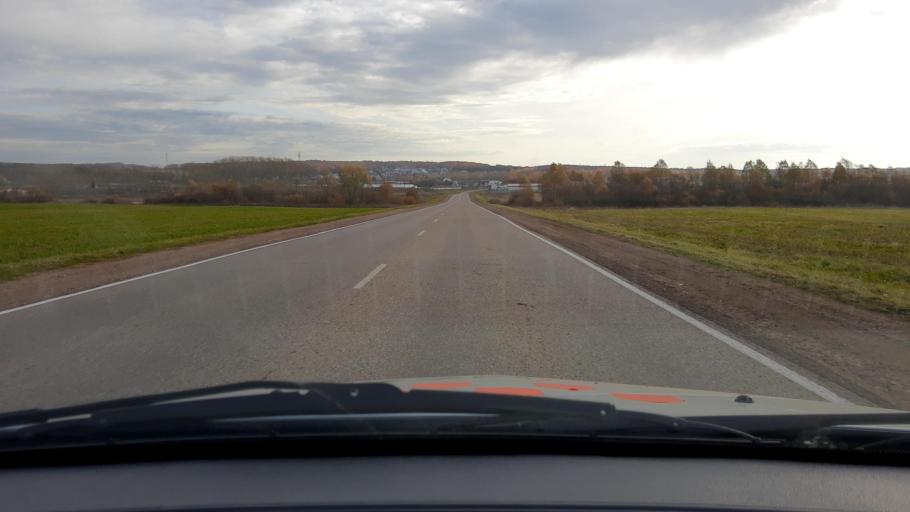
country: RU
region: Bashkortostan
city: Avdon
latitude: 54.8218
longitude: 55.6753
